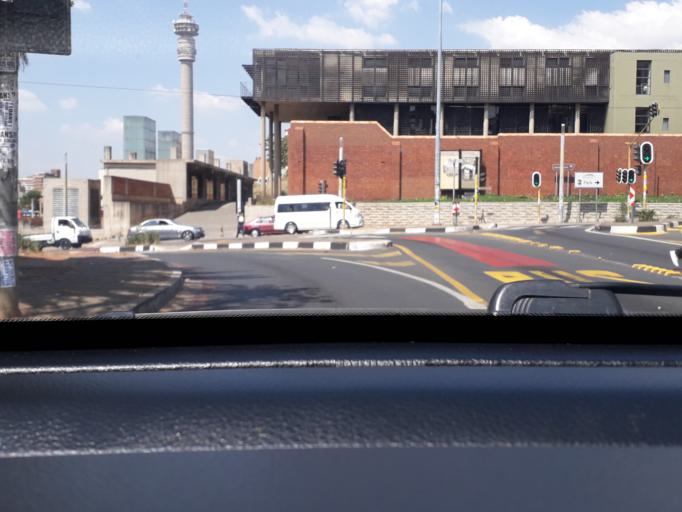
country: ZA
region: Gauteng
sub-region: City of Johannesburg Metropolitan Municipality
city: Johannesburg
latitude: -26.1898
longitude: 28.0407
